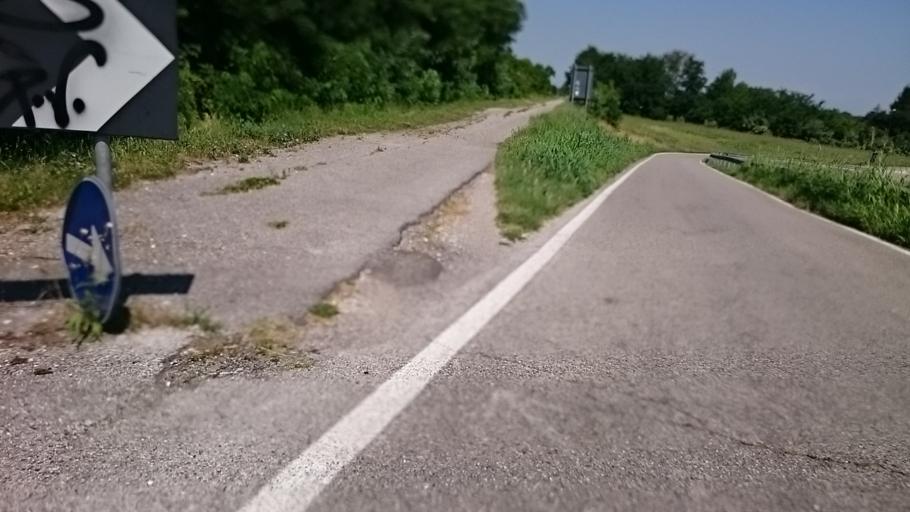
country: IT
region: Veneto
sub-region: Provincia di Venezia
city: Galta
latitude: 45.3839
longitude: 12.0193
